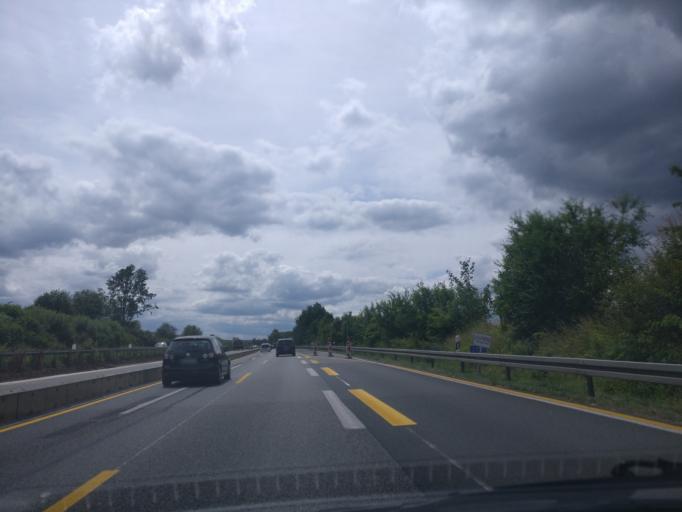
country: DE
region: Lower Saxony
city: Kalefeld
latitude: 51.7779
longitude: 10.0307
